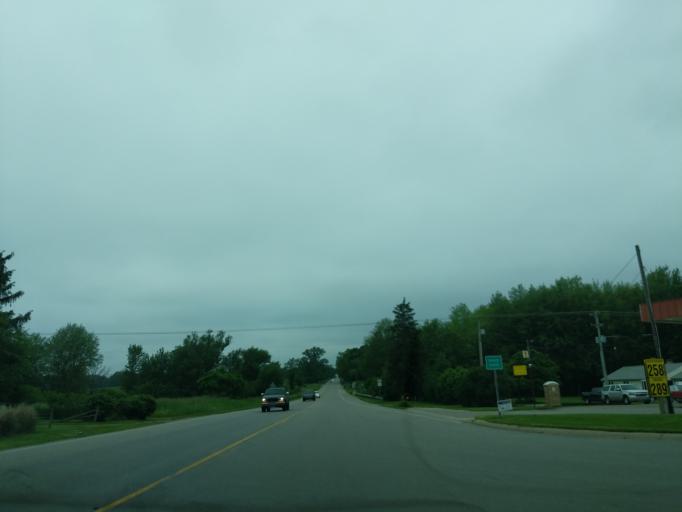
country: US
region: Michigan
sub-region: Branch County
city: Quincy
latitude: 41.9486
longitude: -84.8255
